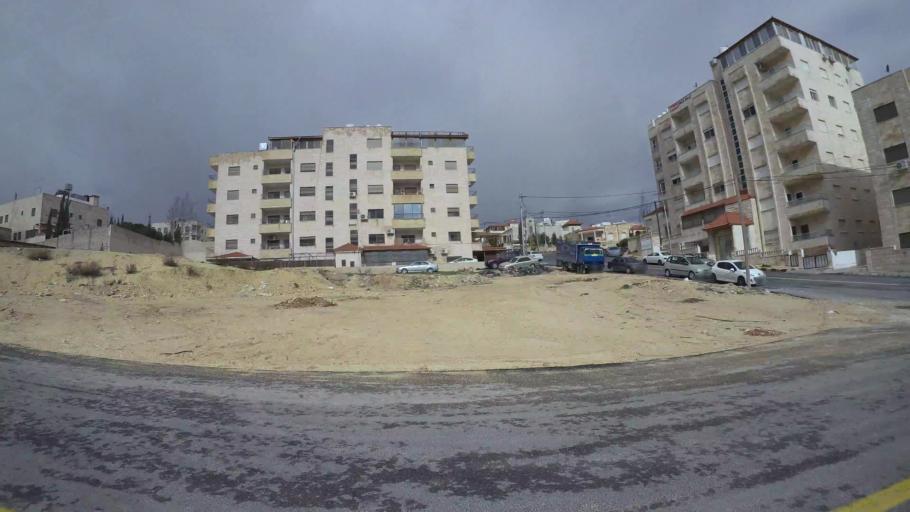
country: JO
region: Amman
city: Al Jubayhah
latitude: 32.0568
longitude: 35.8901
